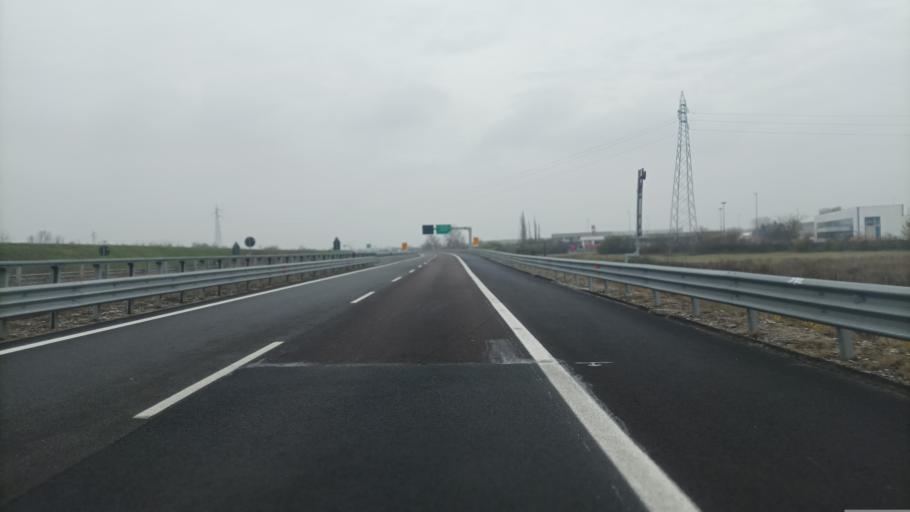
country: IT
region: Emilia-Romagna
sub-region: Provincia di Parma
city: Ponte Taro
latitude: 44.8484
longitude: 10.2260
